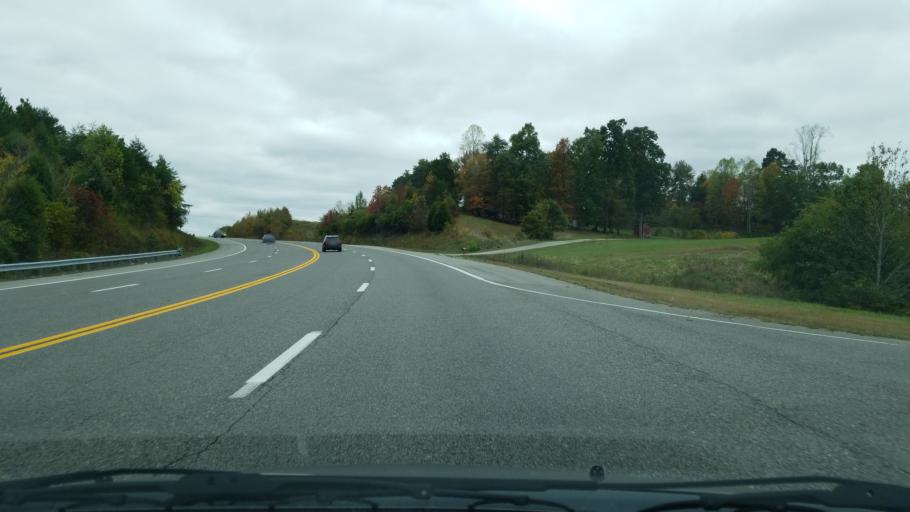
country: US
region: Tennessee
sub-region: Rhea County
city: Dayton
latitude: 35.4699
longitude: -85.0220
